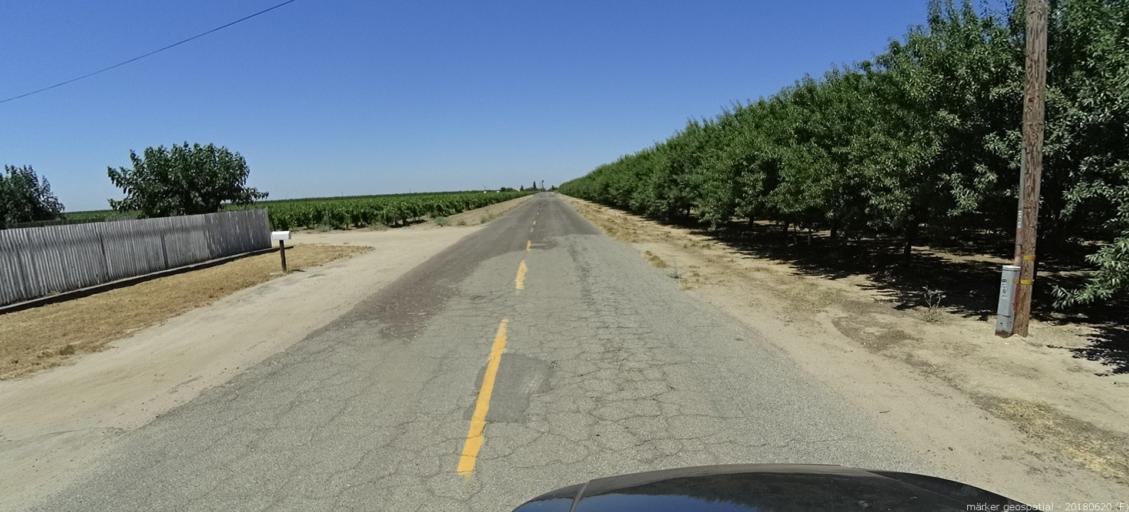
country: US
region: California
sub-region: Madera County
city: Parkwood
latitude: 36.8803
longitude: -120.0294
